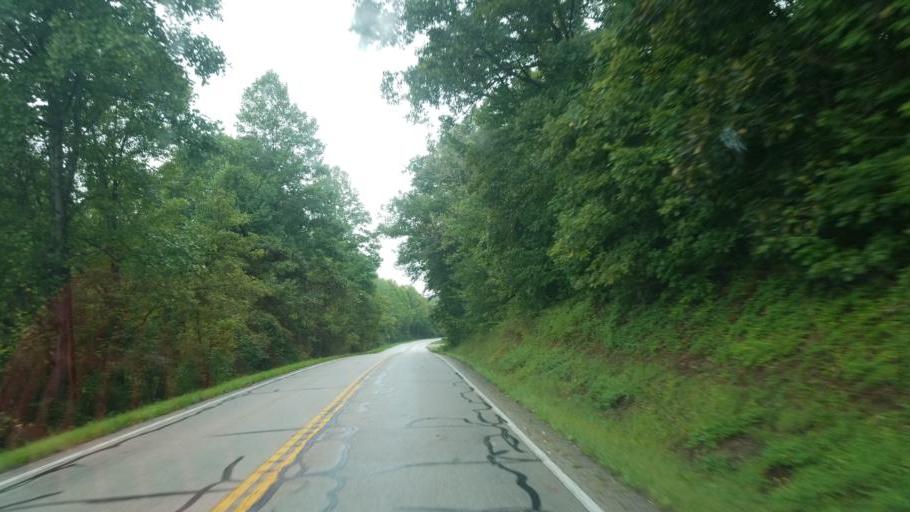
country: US
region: Kentucky
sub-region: Rowan County
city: Morehead
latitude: 38.1510
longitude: -83.4869
